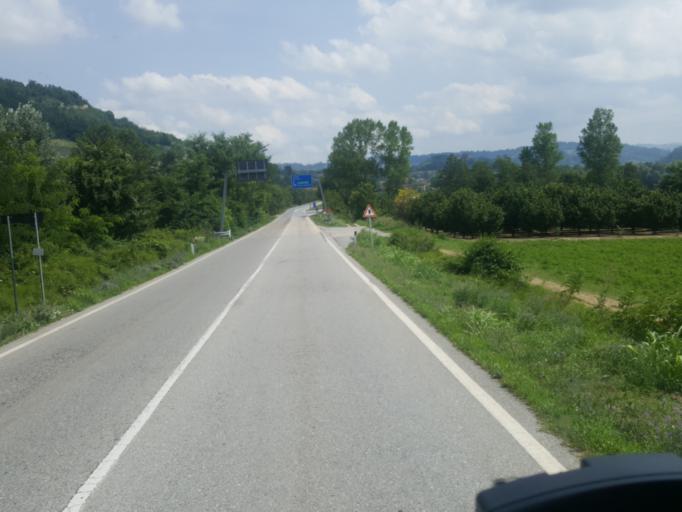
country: IT
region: Piedmont
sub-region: Provincia di Cuneo
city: Monchiero Borgonuovo
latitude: 44.5835
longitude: 7.9048
